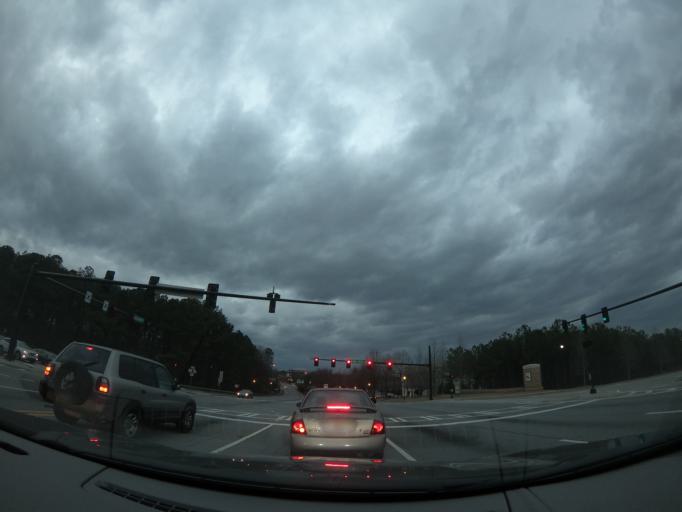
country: US
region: Georgia
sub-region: Fulton County
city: Alpharetta
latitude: 34.0558
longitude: -84.2861
